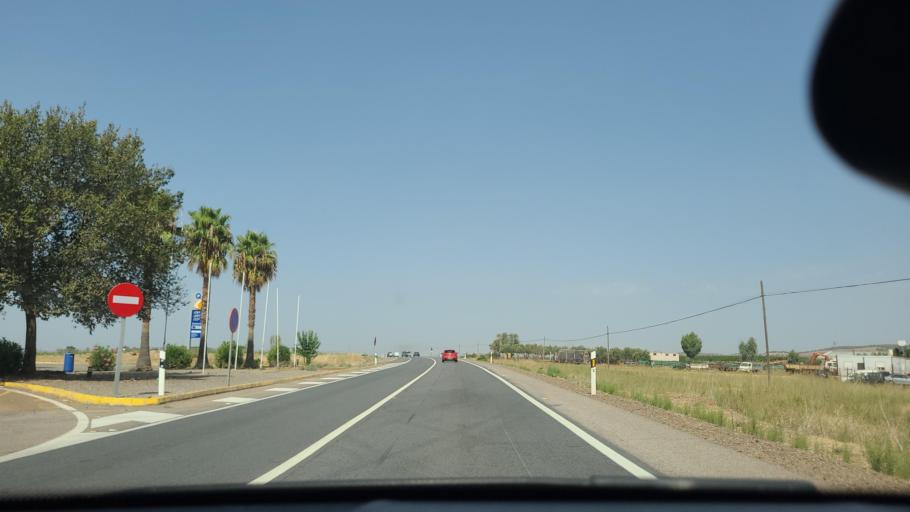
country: ES
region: Extremadura
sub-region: Provincia de Badajoz
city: Puebla de Sancho Perez
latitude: 38.4039
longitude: -6.3599
